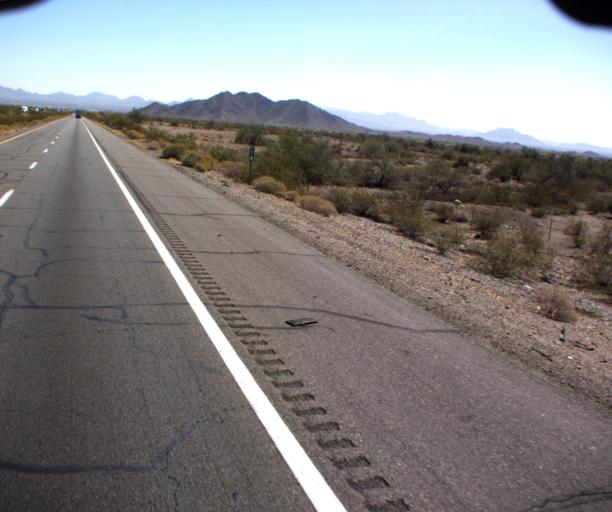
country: US
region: Arizona
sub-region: La Paz County
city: Quartzsite
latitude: 33.6510
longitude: -114.3012
